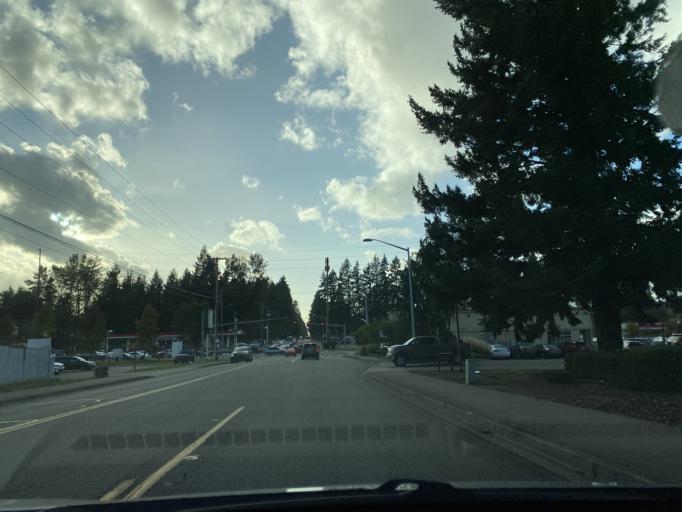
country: US
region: Washington
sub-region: Pierce County
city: South Hill
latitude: 47.1184
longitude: -122.2916
